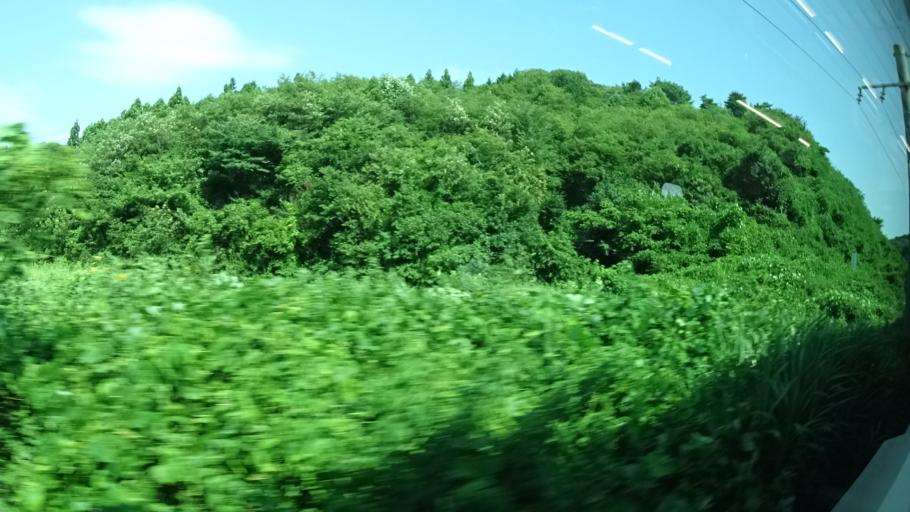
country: JP
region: Miyagi
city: Kogota
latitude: 38.4921
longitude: 141.0882
